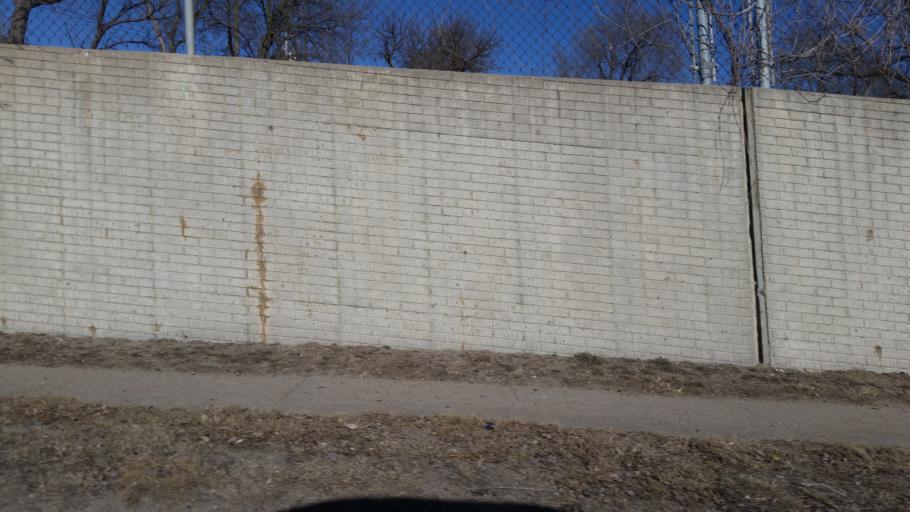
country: US
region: Nebraska
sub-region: Sarpy County
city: Bellevue
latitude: 41.1605
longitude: -95.9209
